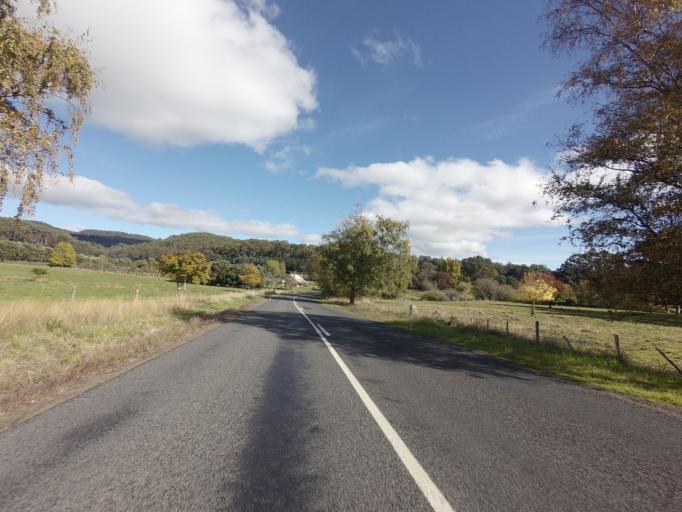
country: AU
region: Tasmania
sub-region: Clarence
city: Sandford
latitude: -43.0626
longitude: 147.8153
